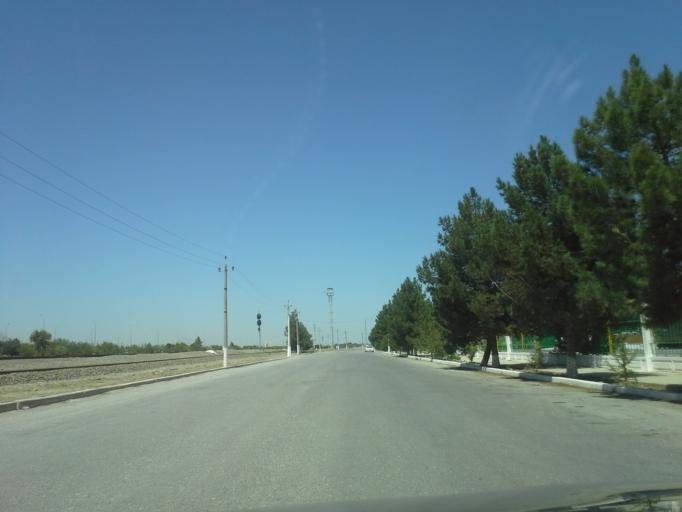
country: TM
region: Ahal
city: Ashgabat
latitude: 37.9938
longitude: 58.3156
